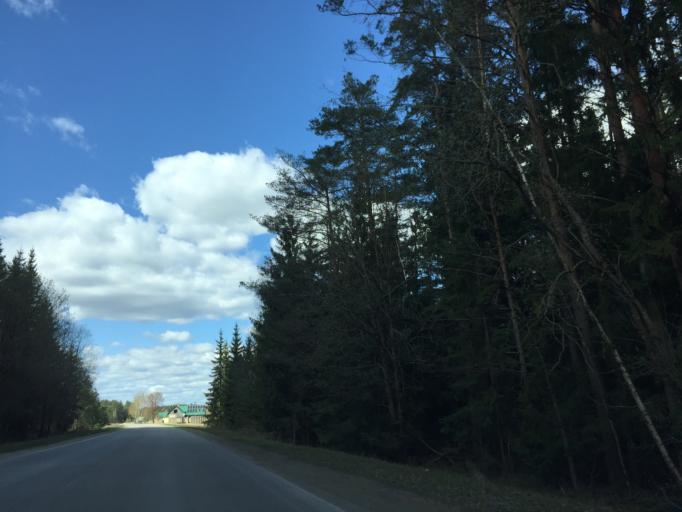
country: LV
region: Vilanu
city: Vilani
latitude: 56.5695
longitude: 27.0485
